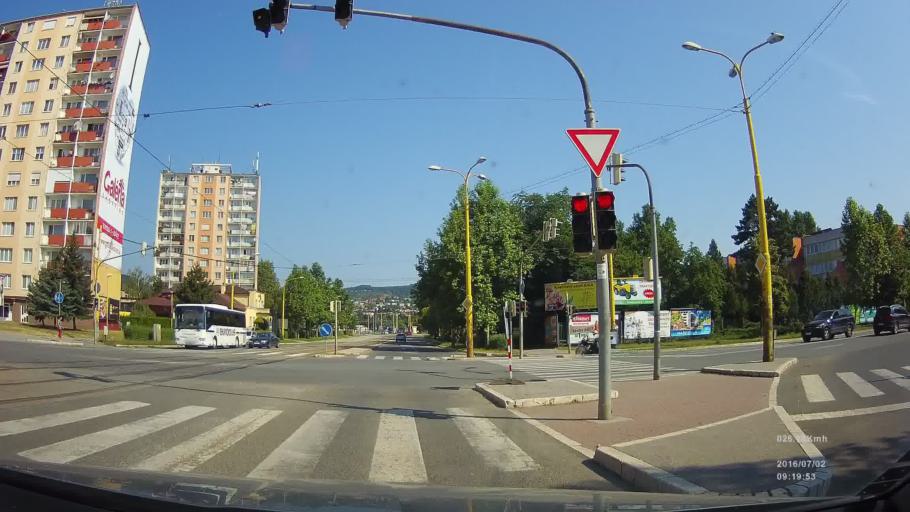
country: SK
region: Kosicky
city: Kosice
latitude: 48.7375
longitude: 21.2399
